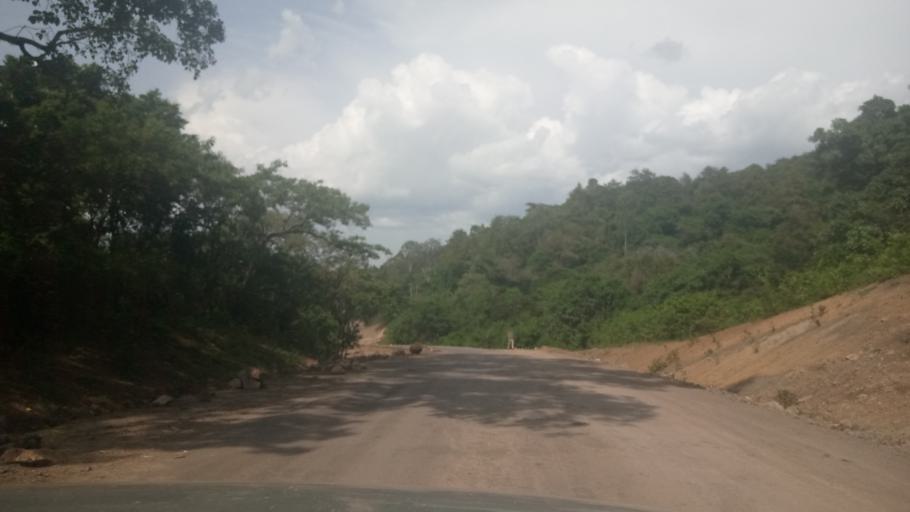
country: ET
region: Oromiya
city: Agaro
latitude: 8.0423
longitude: 36.4693
